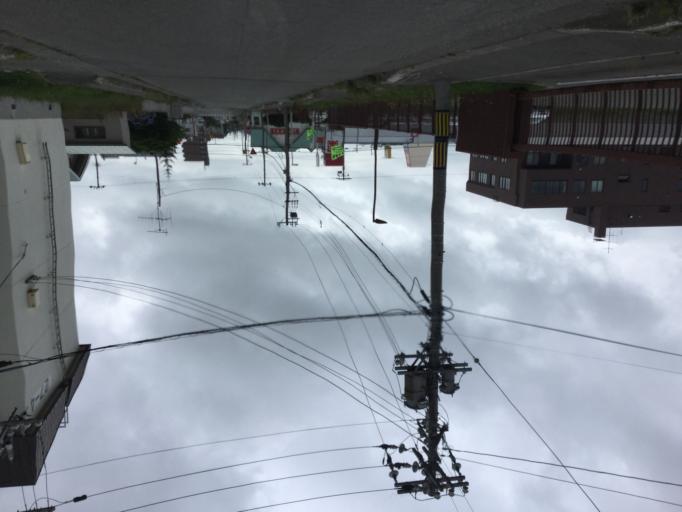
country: JP
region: Hokkaido
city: Wakkanai
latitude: 45.3981
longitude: 141.6990
